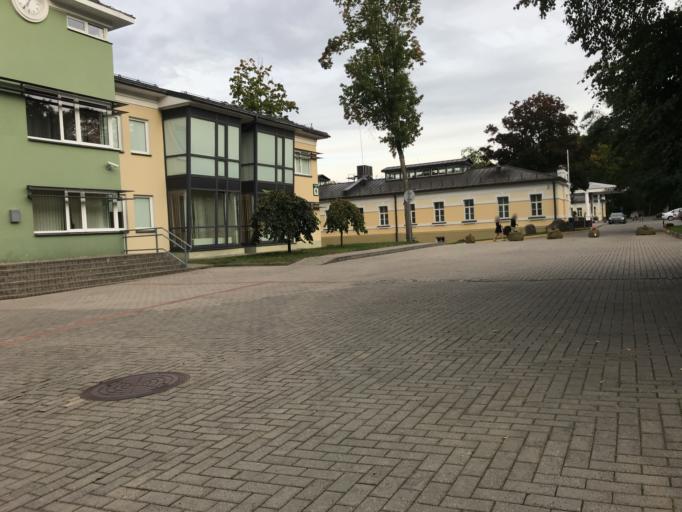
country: LT
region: Alytaus apskritis
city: Druskininkai
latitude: 54.0219
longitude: 23.9752
